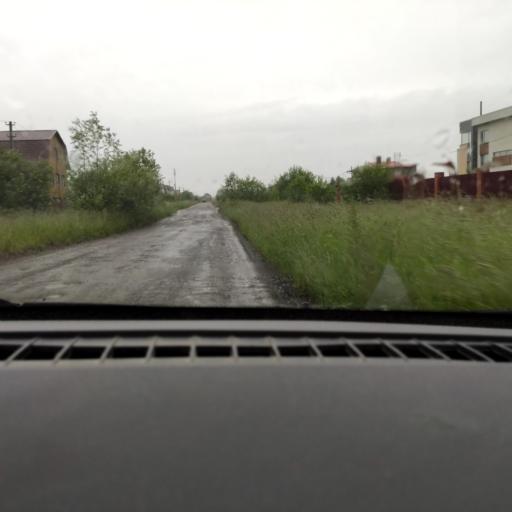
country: RU
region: Perm
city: Perm
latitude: 58.0376
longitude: 56.3718
